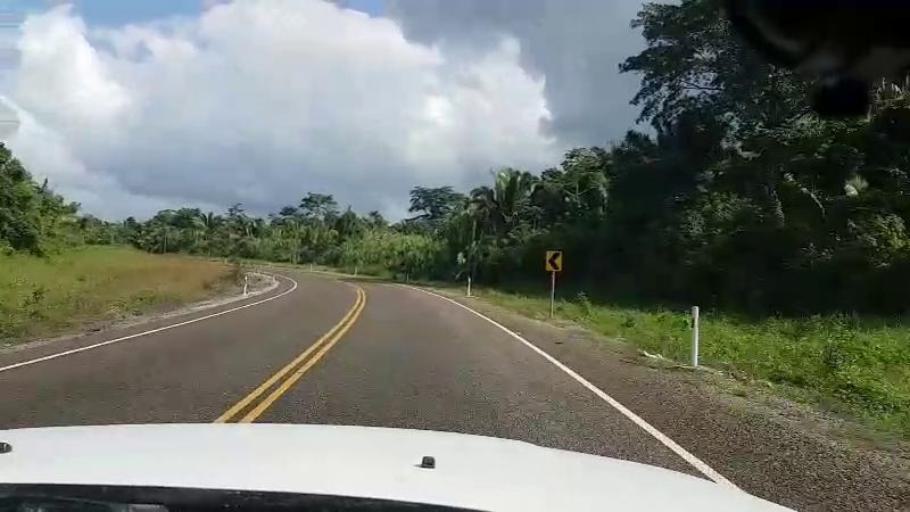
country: BZ
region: Cayo
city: Belmopan
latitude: 17.1458
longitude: -88.7305
